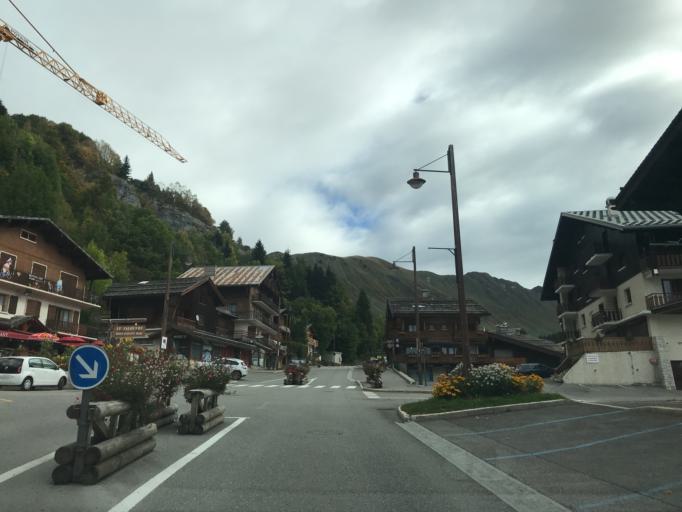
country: FR
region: Rhone-Alpes
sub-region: Departement de la Haute-Savoie
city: Le Grand-Bornand
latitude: 45.9727
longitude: 6.4508
